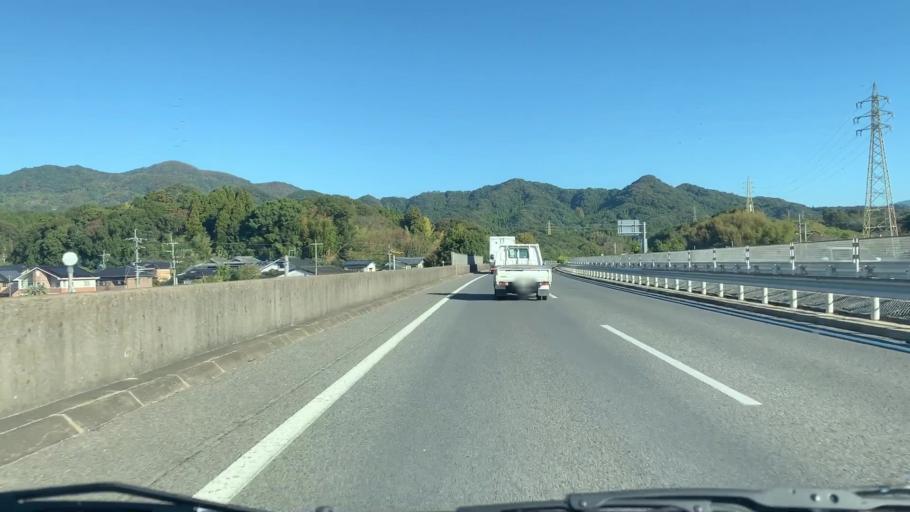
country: JP
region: Saga Prefecture
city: Takeocho-takeo
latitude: 33.2222
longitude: 130.0497
